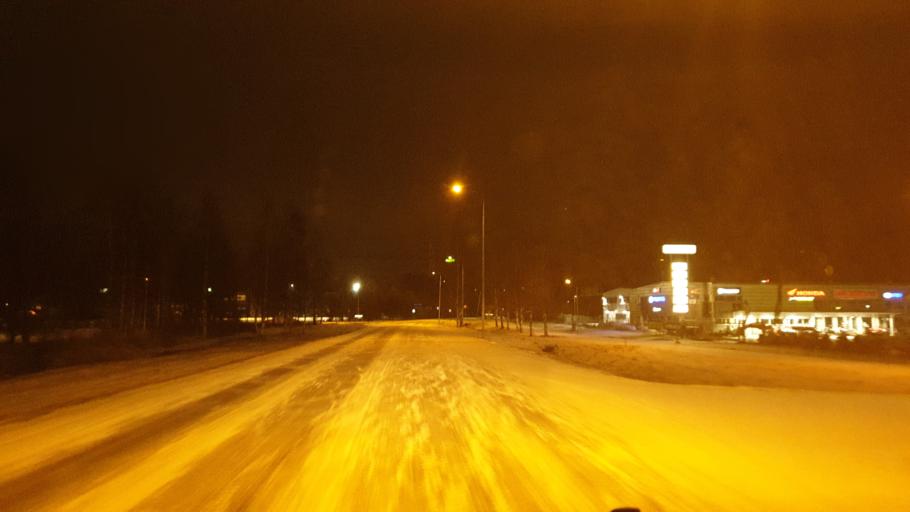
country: FI
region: Northern Ostrobothnia
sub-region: Oulu
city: Oulu
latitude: 64.9951
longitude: 25.4515
